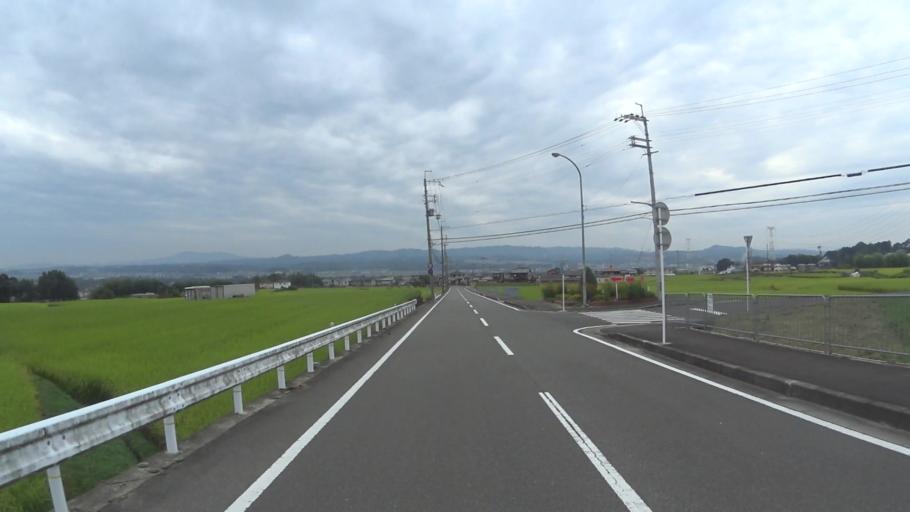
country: JP
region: Kyoto
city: Tanabe
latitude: 34.8016
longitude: 135.8161
